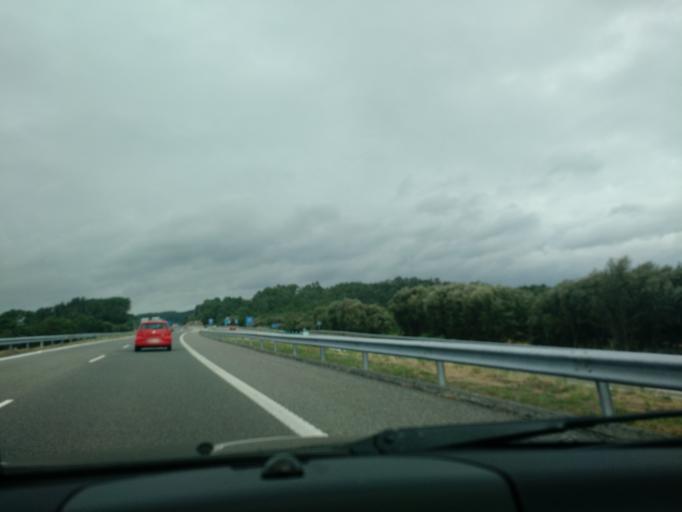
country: ES
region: Galicia
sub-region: Provincia da Coruna
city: Betanzos
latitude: 43.2770
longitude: -8.2628
